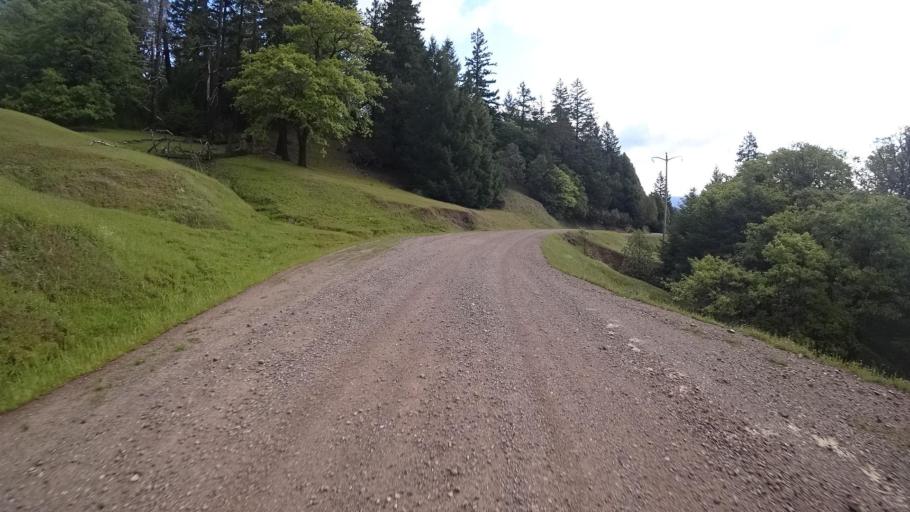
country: US
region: California
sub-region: Humboldt County
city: Redway
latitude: 40.2090
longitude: -123.6844
